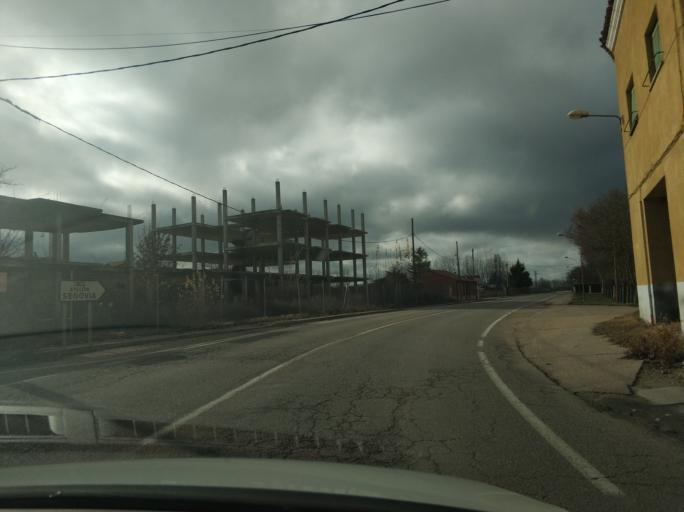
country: ES
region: Castille and Leon
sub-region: Provincia de Soria
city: San Esteban de Gormaz
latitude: 41.5712
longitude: -3.2067
